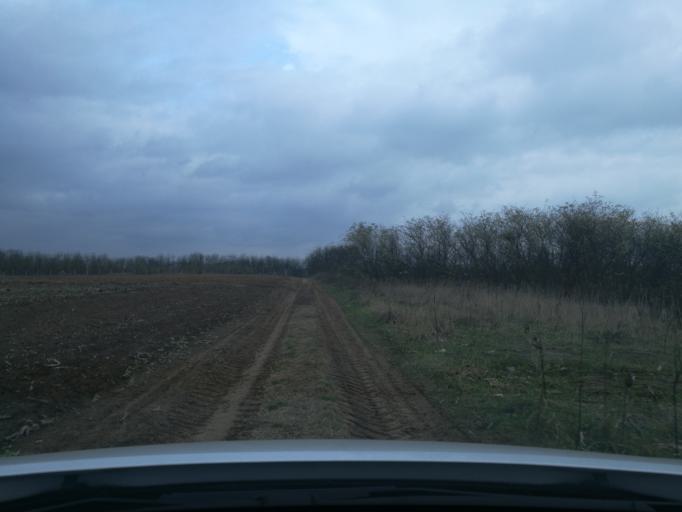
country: HU
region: Szabolcs-Szatmar-Bereg
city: Nyirpazony
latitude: 47.9675
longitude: 21.7851
